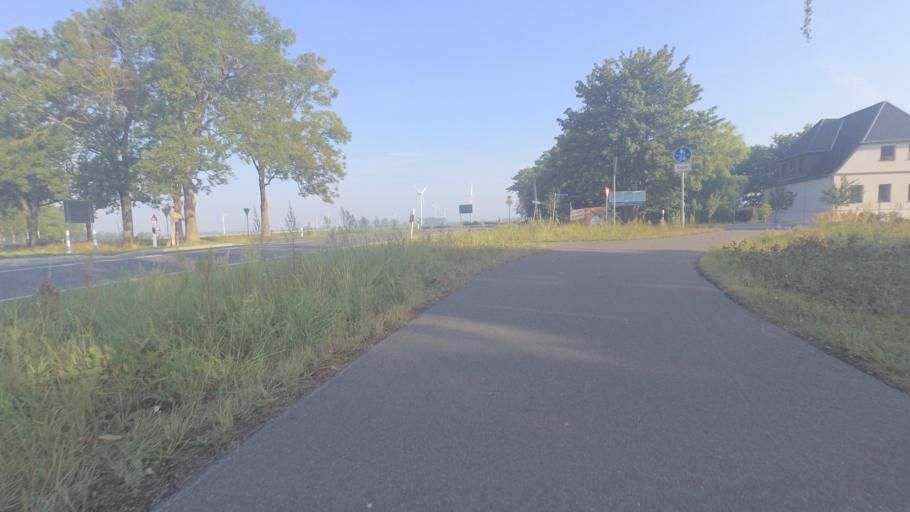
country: DE
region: Mecklenburg-Vorpommern
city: Gormin
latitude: 53.9970
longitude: 13.1471
